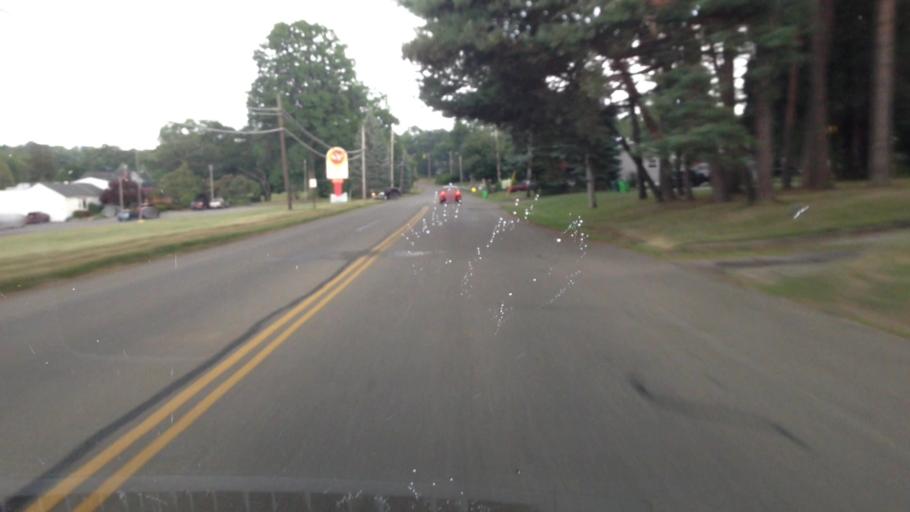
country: US
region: Ohio
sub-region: Summit County
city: Barberton
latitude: 41.0202
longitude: -81.5813
